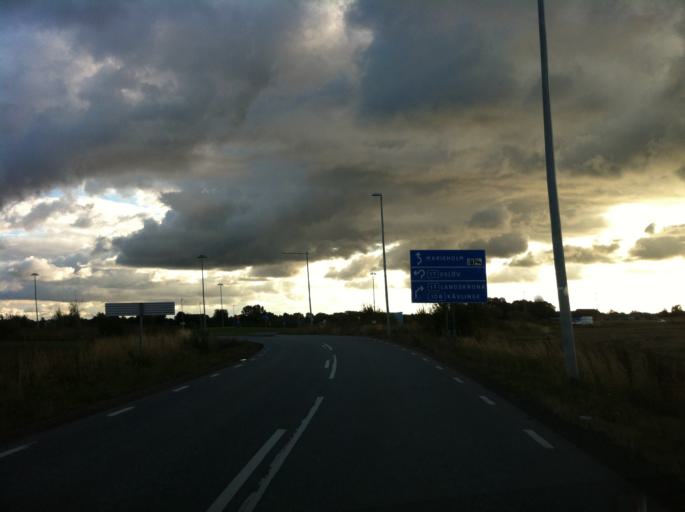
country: SE
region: Skane
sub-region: Svalovs Kommun
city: Svaloev
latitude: 55.8782
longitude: 13.1642
